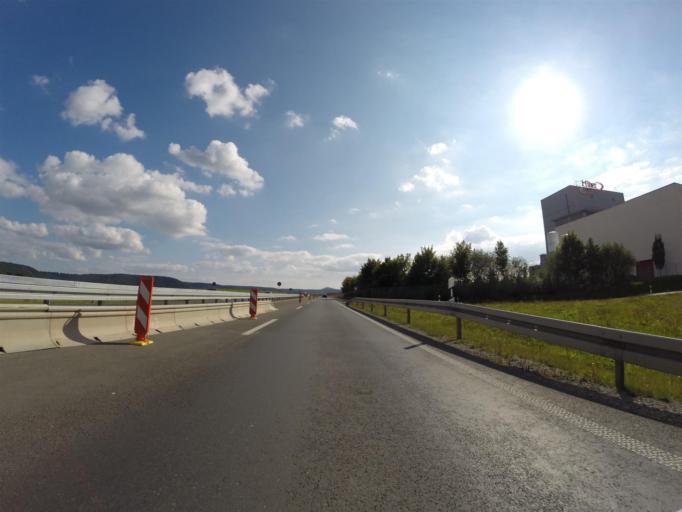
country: DE
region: Thuringia
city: Rothenstein
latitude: 50.8616
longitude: 11.5983
